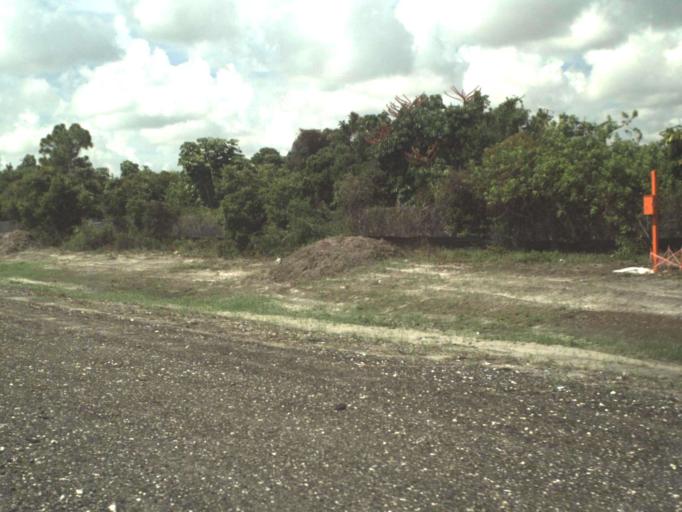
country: US
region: Florida
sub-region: Palm Beach County
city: Highland Beach
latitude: 26.4021
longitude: -80.0902
